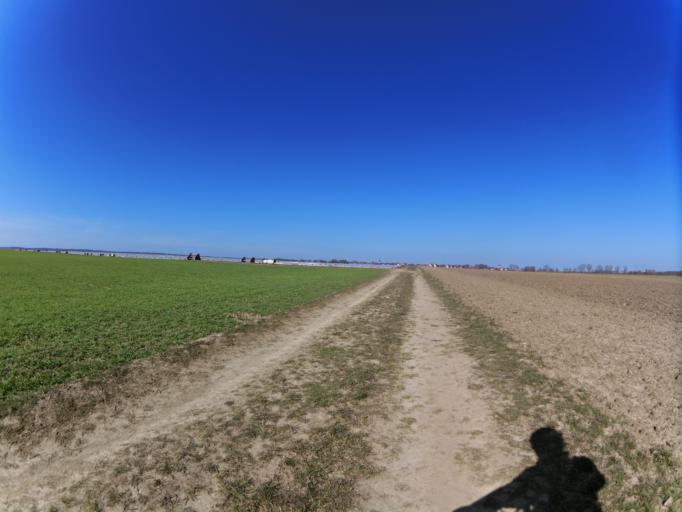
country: DE
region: Bavaria
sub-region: Regierungsbezirk Unterfranken
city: Oberpleichfeld
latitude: 49.8864
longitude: 10.0831
